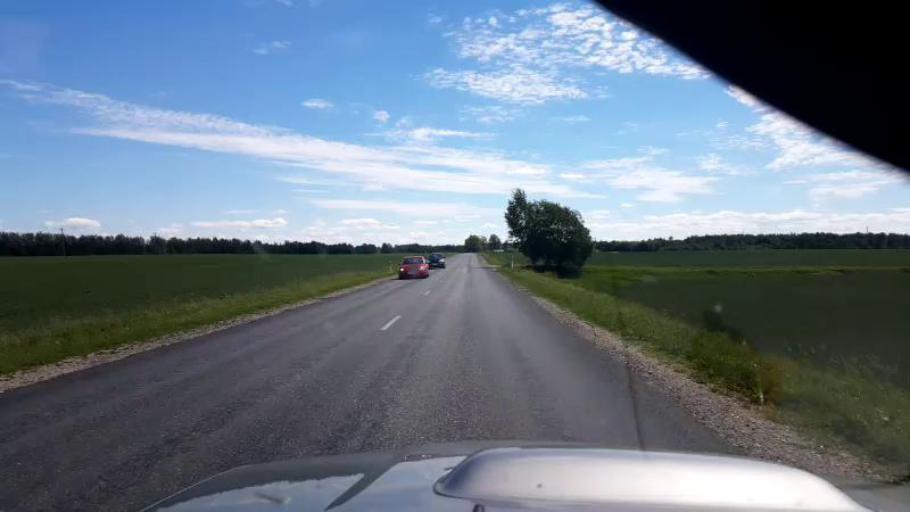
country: EE
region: Laeaene-Virumaa
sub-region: Rakke vald
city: Rakke
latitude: 58.8946
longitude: 26.2840
